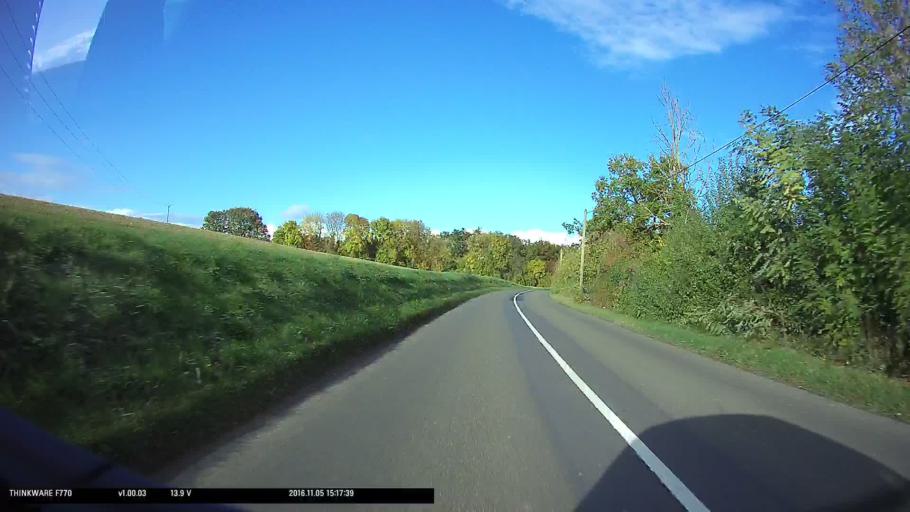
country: FR
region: Ile-de-France
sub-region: Departement du Val-d'Oise
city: Ableiges
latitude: 49.0848
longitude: 1.9781
